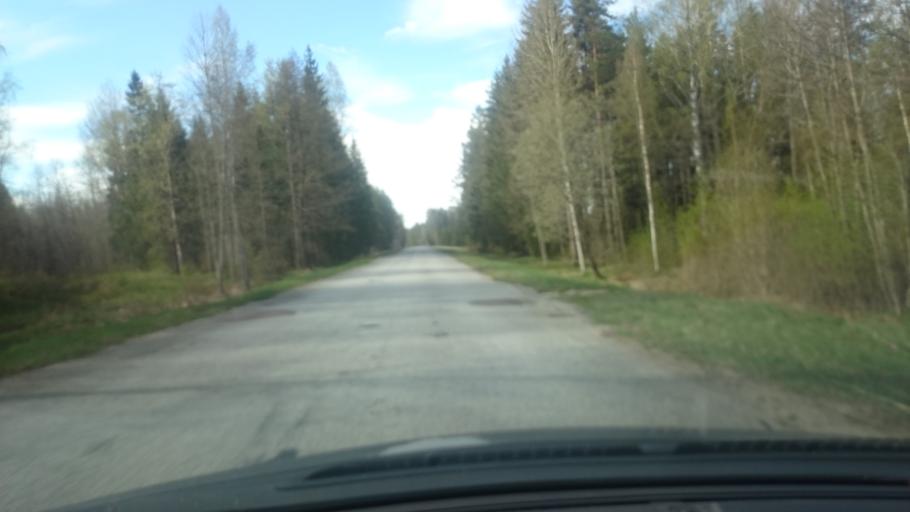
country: EE
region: Ida-Virumaa
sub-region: Toila vald
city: Voka
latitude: 59.1486
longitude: 27.6091
